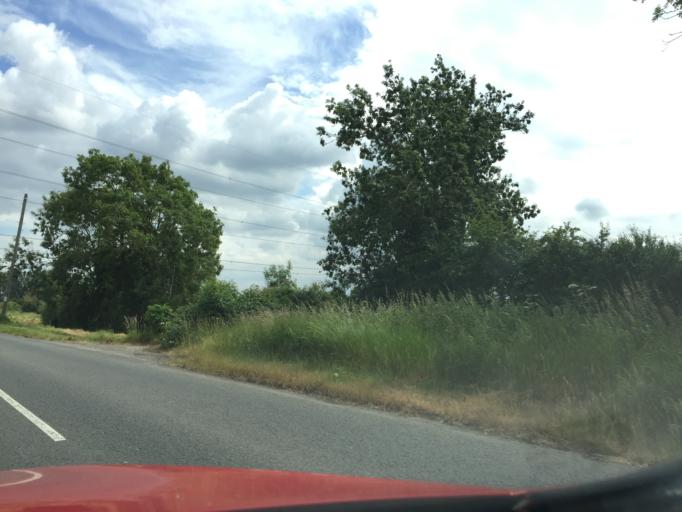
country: GB
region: England
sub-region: South Gloucestershire
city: Severn Beach
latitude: 51.5556
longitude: -2.6351
